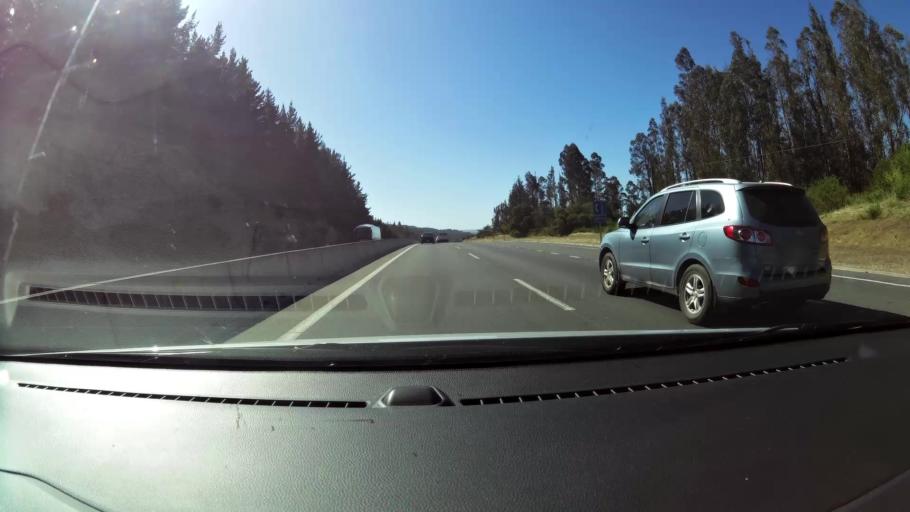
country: CL
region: Valparaiso
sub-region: Provincia de Marga Marga
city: Quilpue
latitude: -33.2047
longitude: -71.4850
